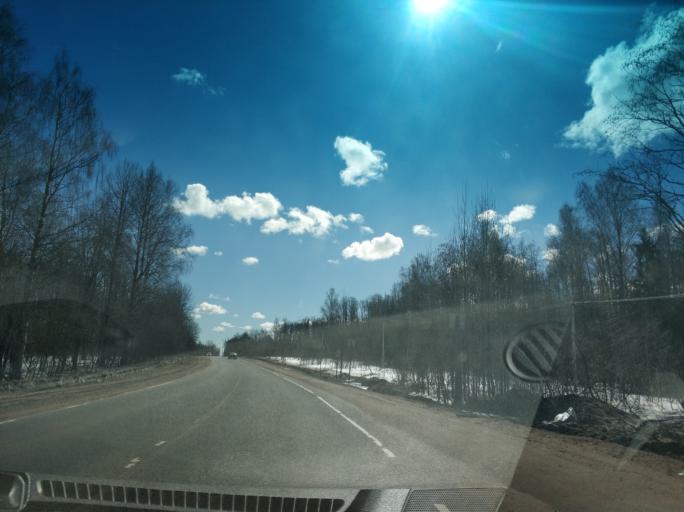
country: RU
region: Leningrad
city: Sosnovo
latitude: 60.4430
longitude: 30.2346
